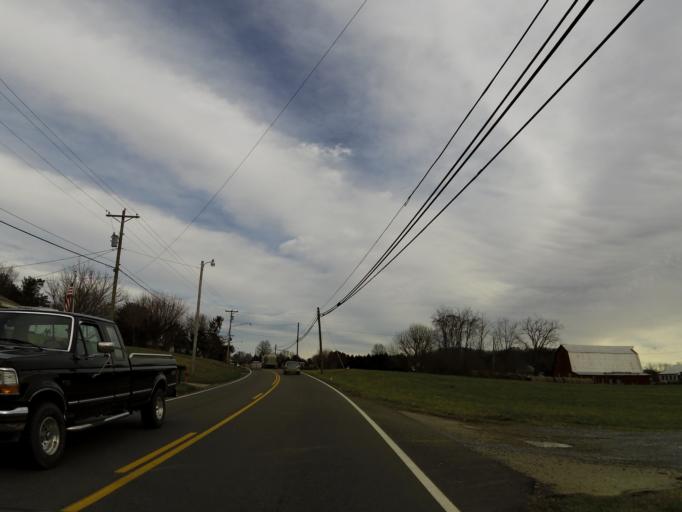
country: US
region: Tennessee
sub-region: Greene County
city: Greeneville
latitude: 36.1421
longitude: -82.8672
